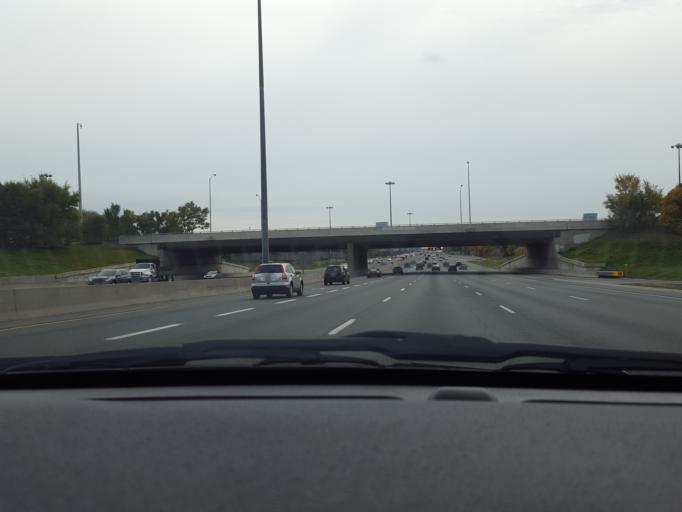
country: CA
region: Ontario
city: Willowdale
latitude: 43.7964
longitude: -79.3441
